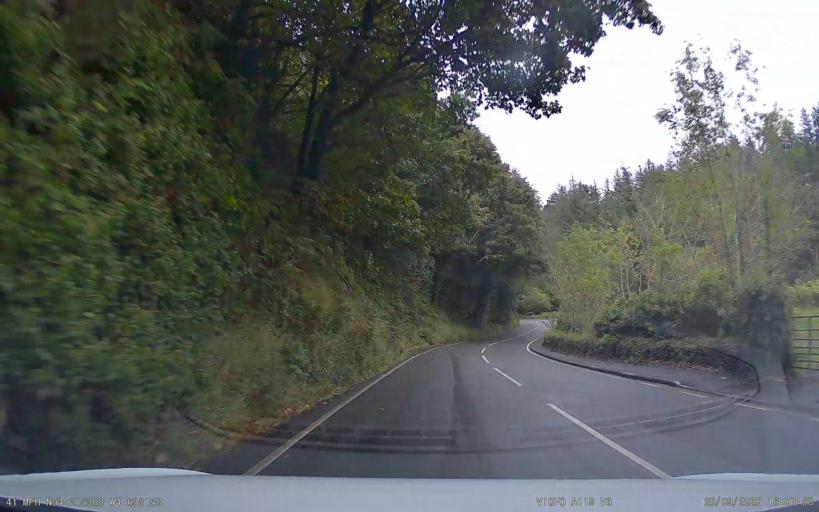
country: IM
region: Castletown
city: Castletown
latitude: 54.2153
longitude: -4.6332
